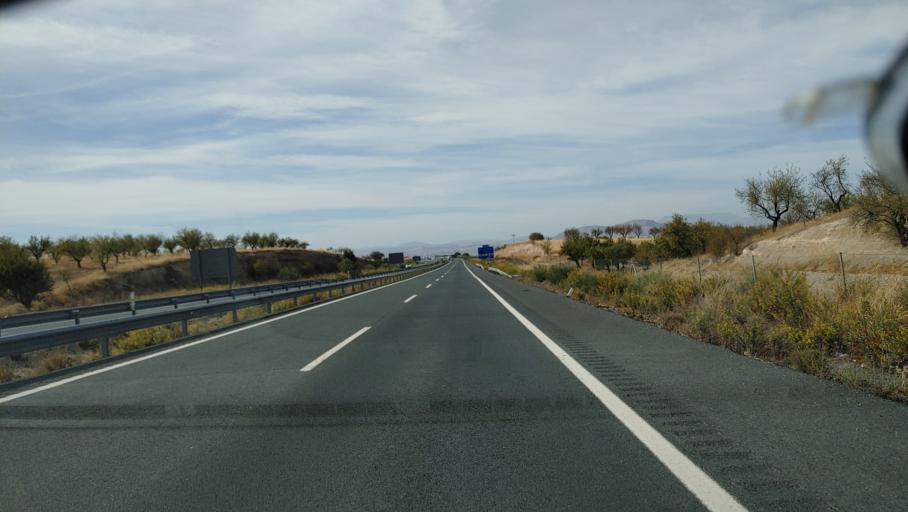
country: ES
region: Andalusia
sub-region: Provincia de Granada
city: Gor
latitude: 37.3897
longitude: -3.0132
